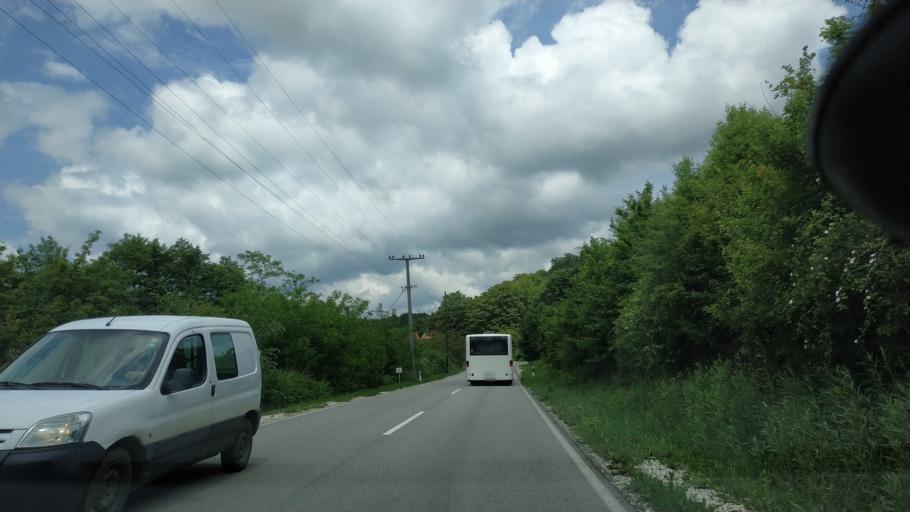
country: RS
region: Central Serbia
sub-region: Borski Okrug
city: Bor
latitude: 44.0526
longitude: 22.0715
